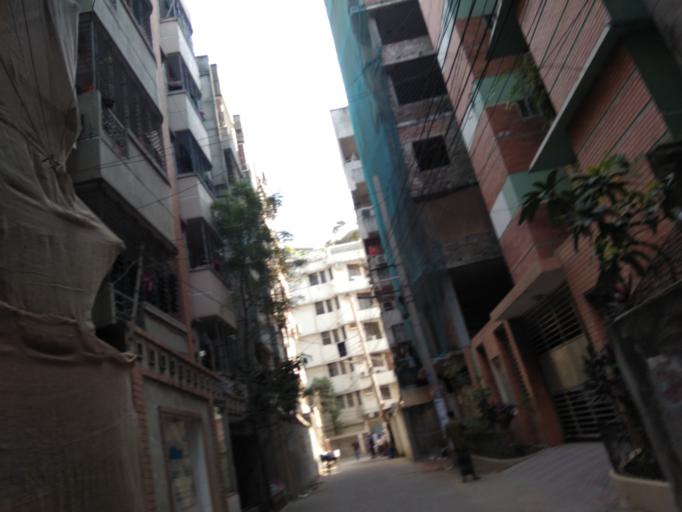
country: BD
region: Dhaka
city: Azimpur
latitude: 23.7705
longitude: 90.3570
